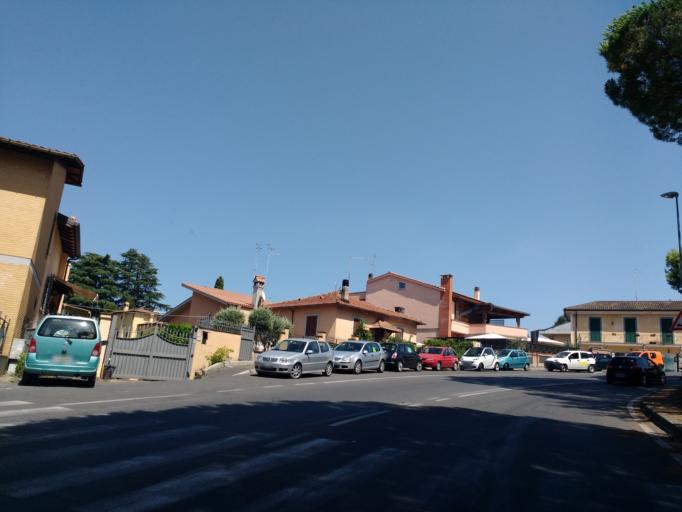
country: IT
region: Latium
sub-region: Citta metropolitana di Roma Capitale
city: Grottaferrata
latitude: 41.7821
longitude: 12.6833
